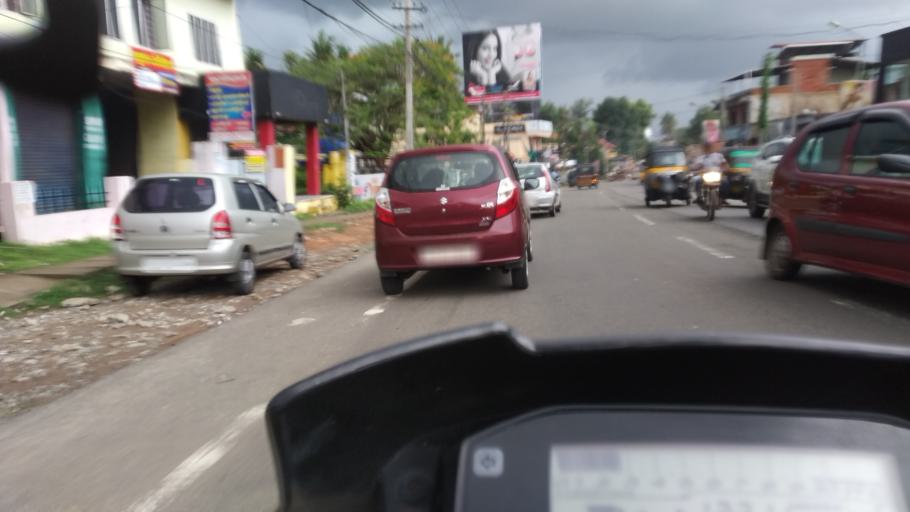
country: IN
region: Kerala
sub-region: Thiruvananthapuram
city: Attingal
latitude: 8.7009
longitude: 76.8136
